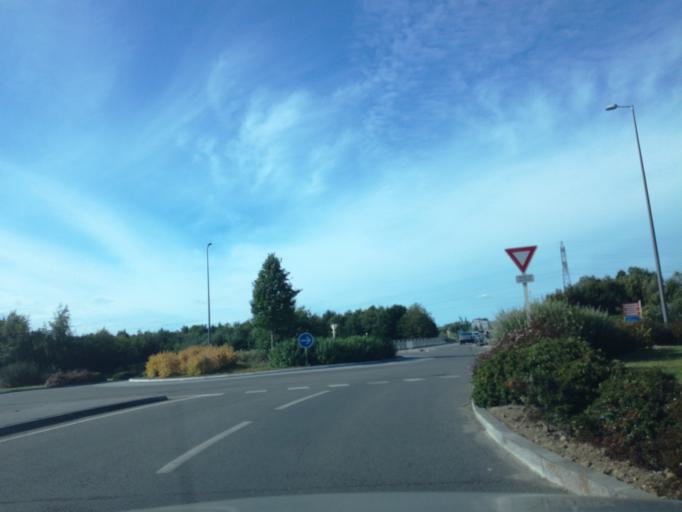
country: FR
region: Brittany
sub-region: Departement d'Ille-et-Vilaine
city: Saint-Gregoire
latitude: 48.1401
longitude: -1.6865
